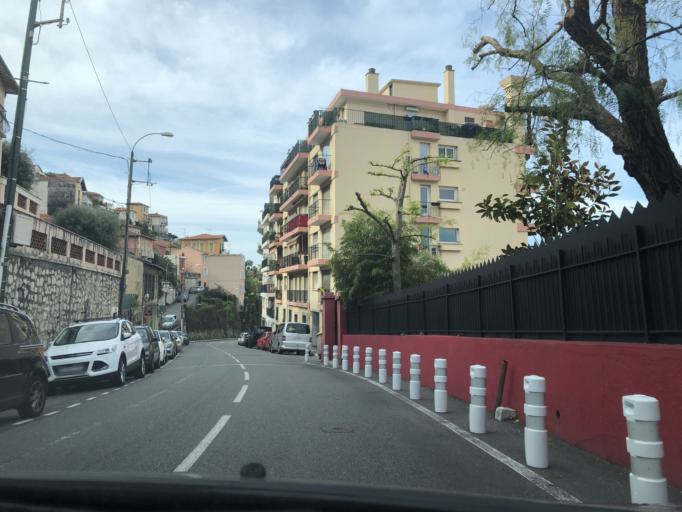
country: FR
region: Provence-Alpes-Cote d'Azur
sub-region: Departement des Alpes-Maritimes
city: Villefranche-sur-Mer
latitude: 43.7129
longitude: 7.2959
